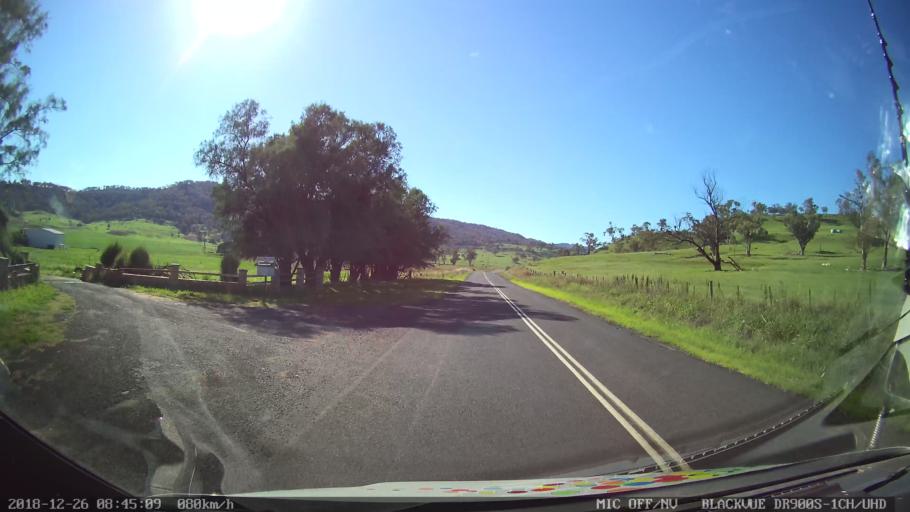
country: AU
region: New South Wales
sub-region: Mid-Western Regional
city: Kandos
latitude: -32.5223
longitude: 150.0845
